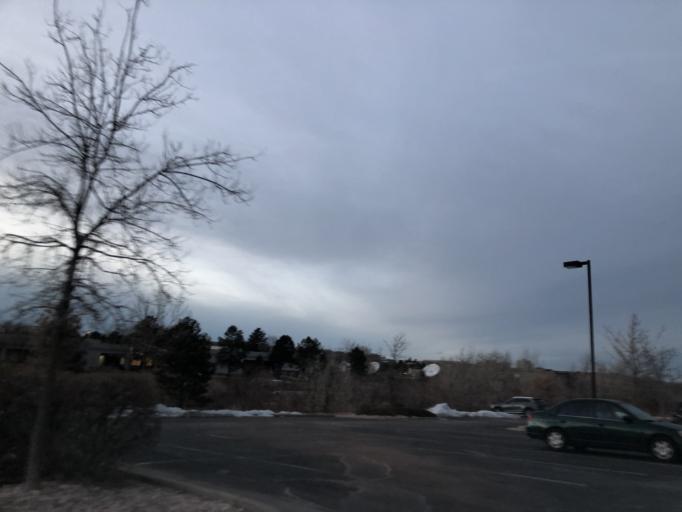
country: US
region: Colorado
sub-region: Douglas County
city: Meridian
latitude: 39.5585
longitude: -104.8611
